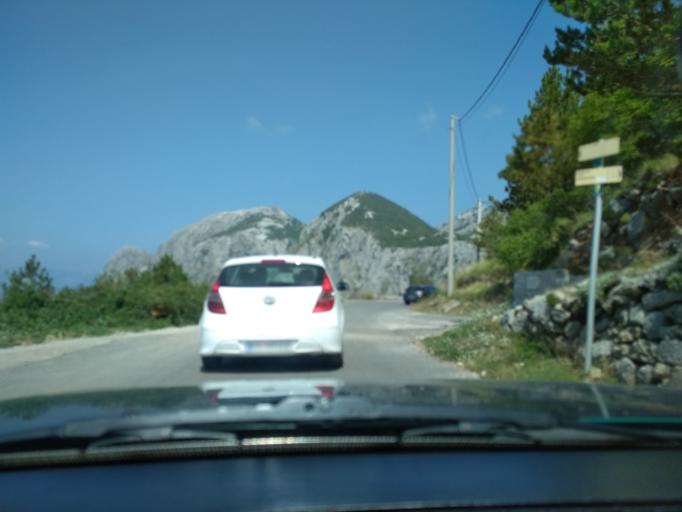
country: ME
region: Kotor
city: Kotor
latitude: 42.4204
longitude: 18.7945
